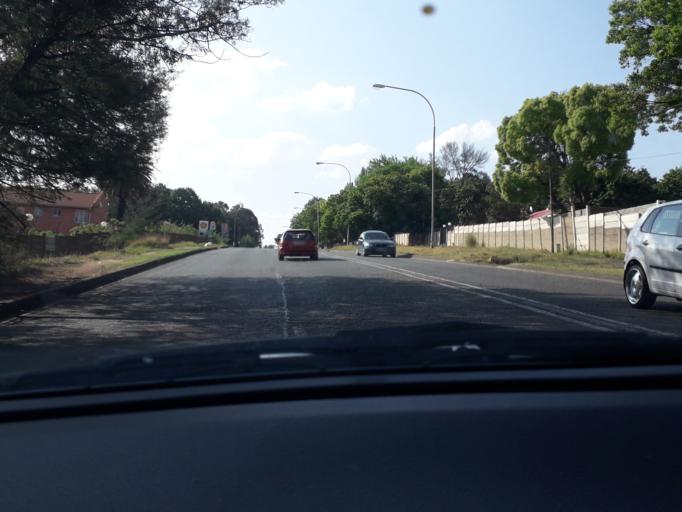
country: ZA
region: Gauteng
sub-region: City of Johannesburg Metropolitan Municipality
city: Modderfontein
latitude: -26.1263
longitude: 28.1242
